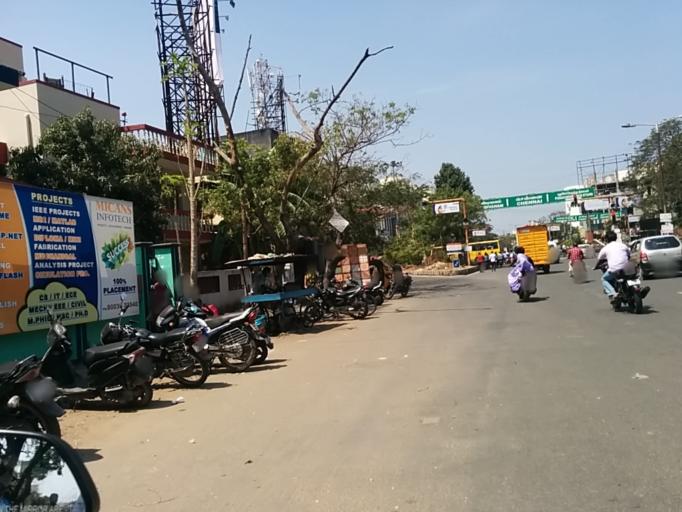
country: IN
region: Pondicherry
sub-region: Puducherry
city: Puducherry
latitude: 11.9307
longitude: 79.8076
